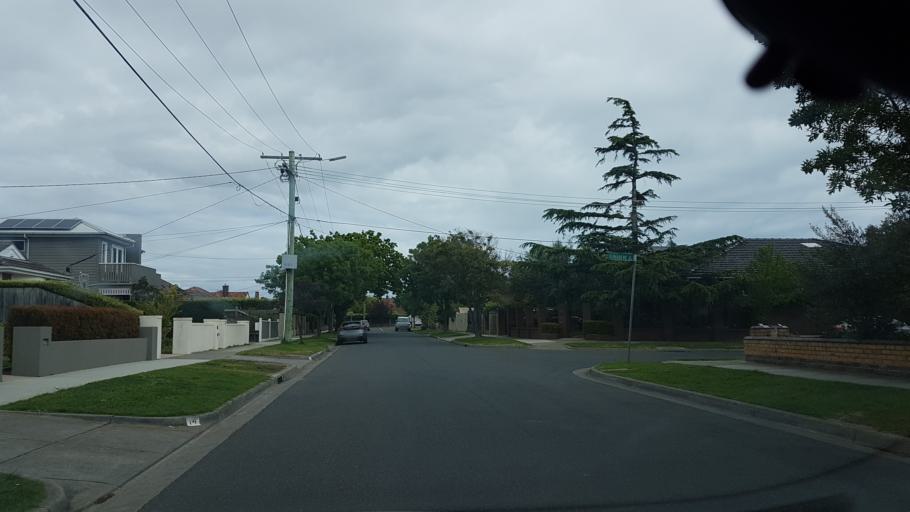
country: AU
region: Victoria
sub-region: Glen Eira
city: Bentleigh
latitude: -37.9238
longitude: 145.0295
